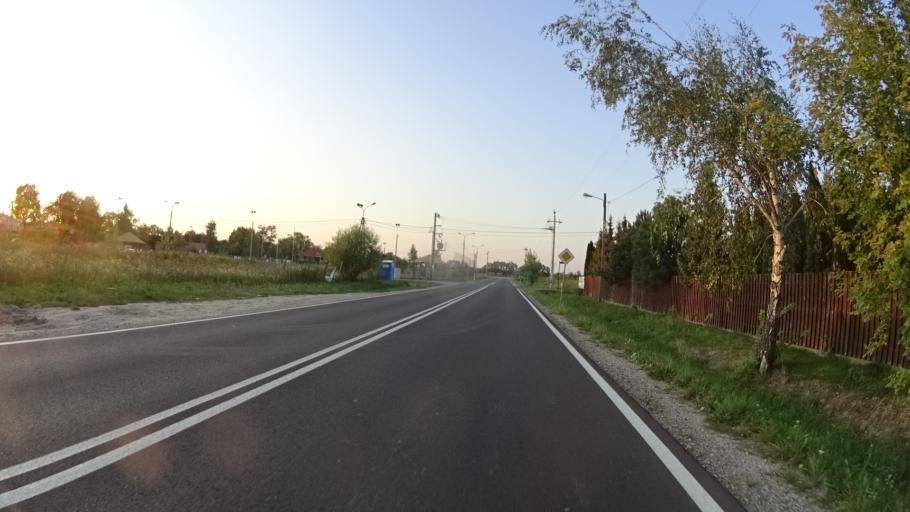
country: PL
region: Masovian Voivodeship
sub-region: Powiat warszawski zachodni
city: Truskaw
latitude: 52.2513
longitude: 20.7412
